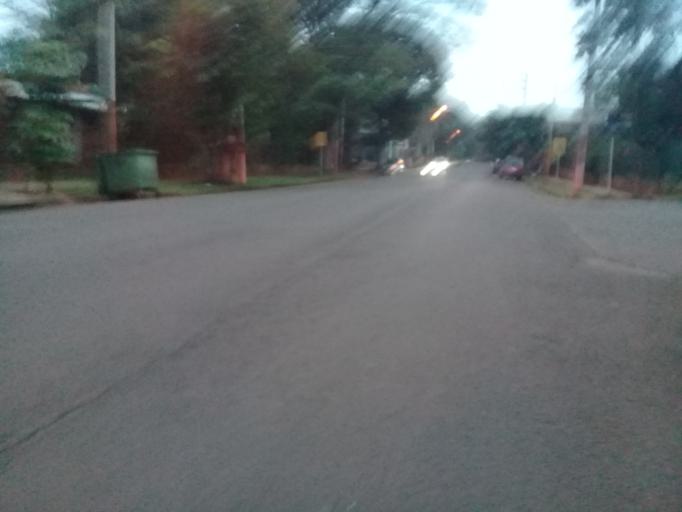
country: AR
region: Misiones
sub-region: Departamento de Iguazu
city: Puerto Iguazu
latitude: -25.5969
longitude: -54.5707
